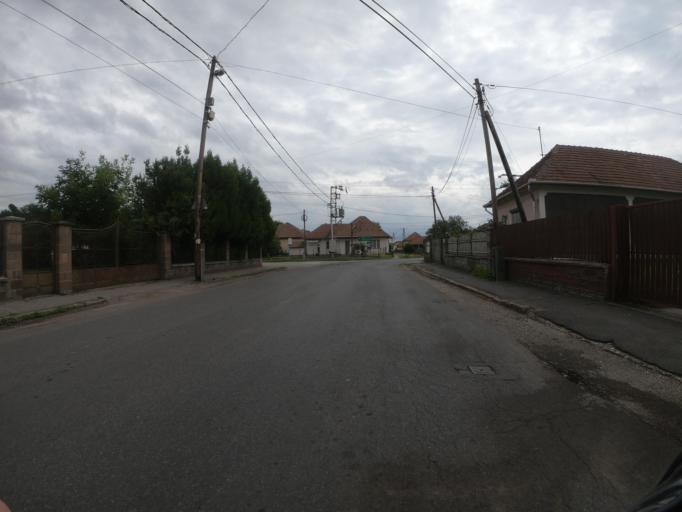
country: HU
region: Borsod-Abauj-Zemplen
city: Szentistvan
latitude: 47.7735
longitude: 20.6605
